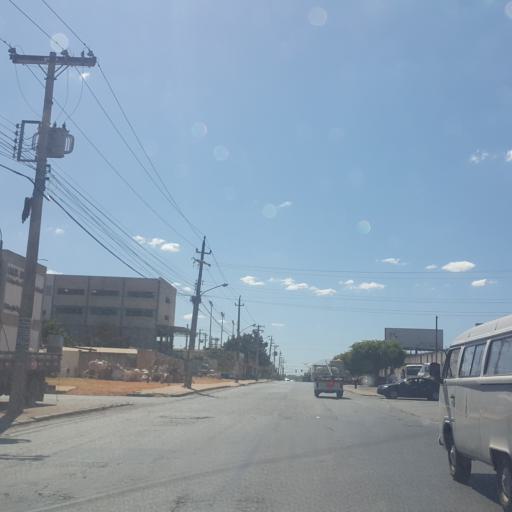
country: BR
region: Federal District
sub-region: Brasilia
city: Brasilia
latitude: -15.8081
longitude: -48.0738
